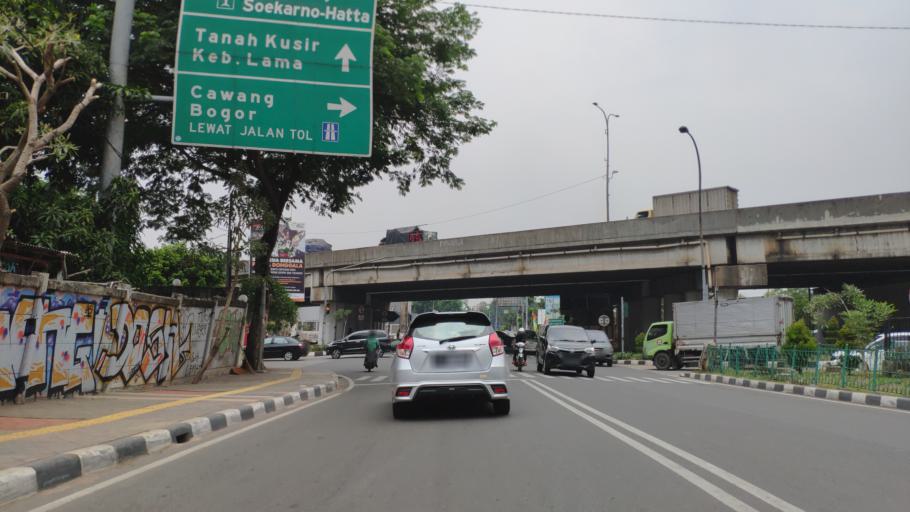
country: ID
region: Banten
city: South Tangerang
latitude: -6.2622
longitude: 106.7667
